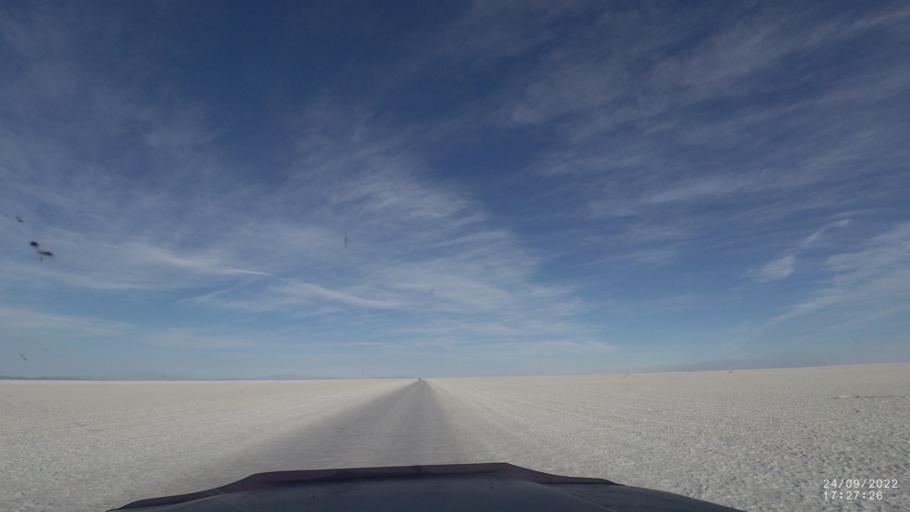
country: BO
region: Potosi
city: Colchani
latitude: -20.2998
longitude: -67.4487
